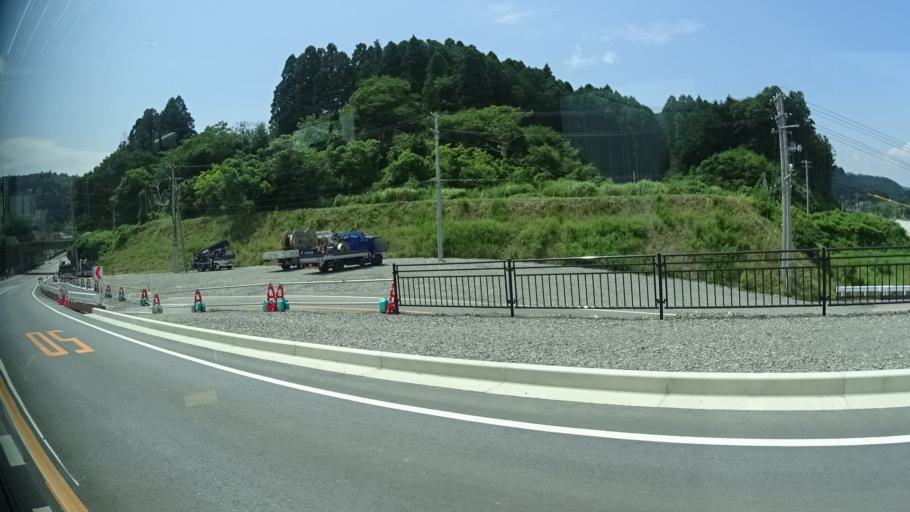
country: JP
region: Miyagi
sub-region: Oshika Gun
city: Onagawa Cho
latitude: 38.6731
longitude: 141.4431
